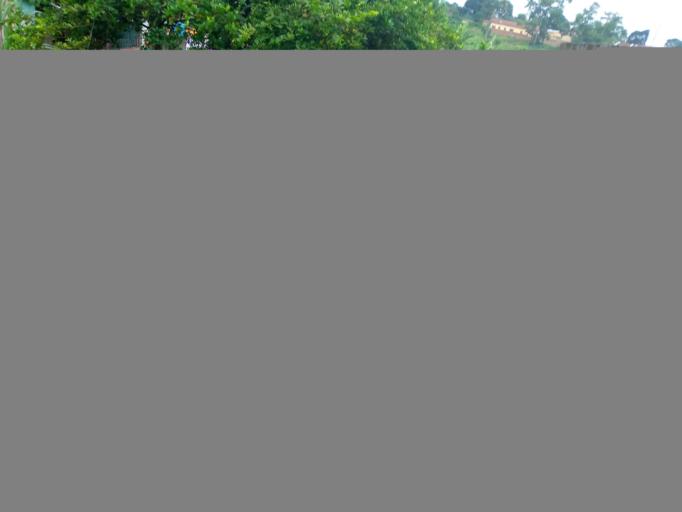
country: SL
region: Eastern Province
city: Kenema
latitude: 7.8680
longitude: -11.1864
